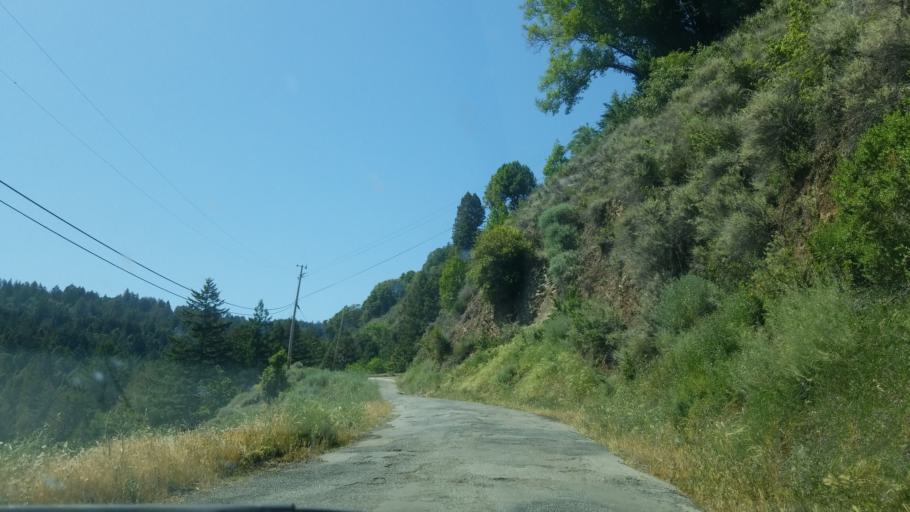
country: US
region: California
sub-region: Santa Cruz County
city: Day Valley
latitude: 37.0629
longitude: -121.8268
